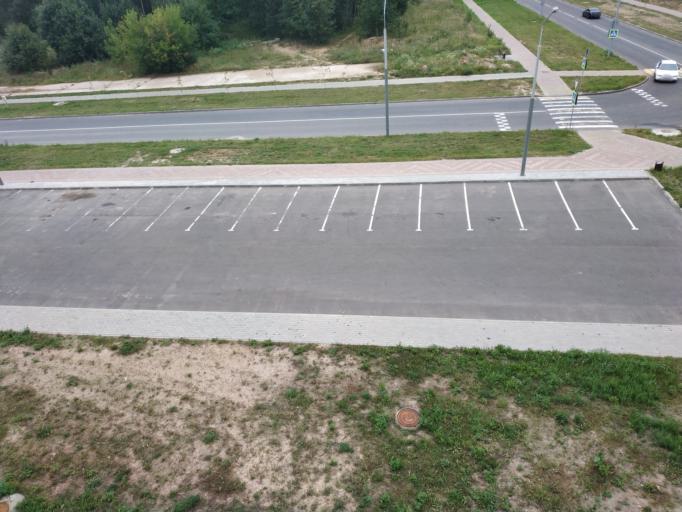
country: BY
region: Vitebsk
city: Navapolatsk
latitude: 55.5120
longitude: 28.6841
